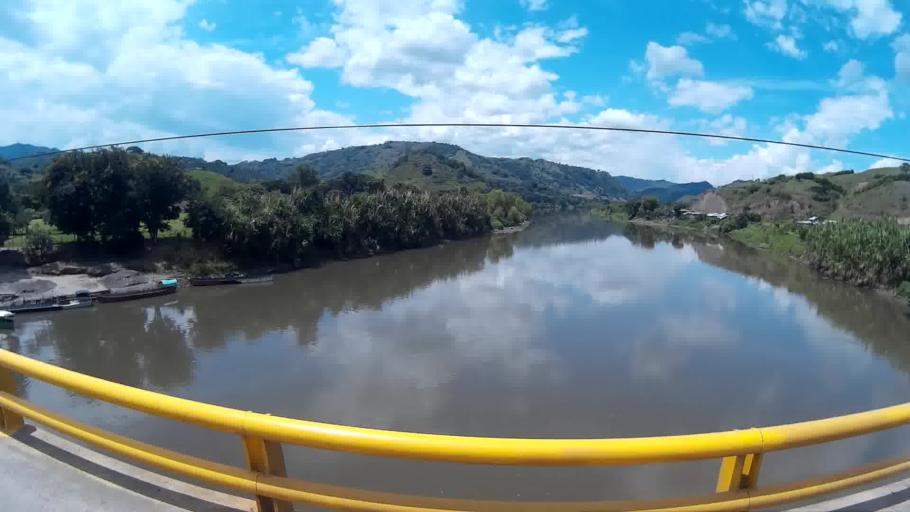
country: CO
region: Risaralda
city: La Virginia
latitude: 4.8841
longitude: -75.8698
